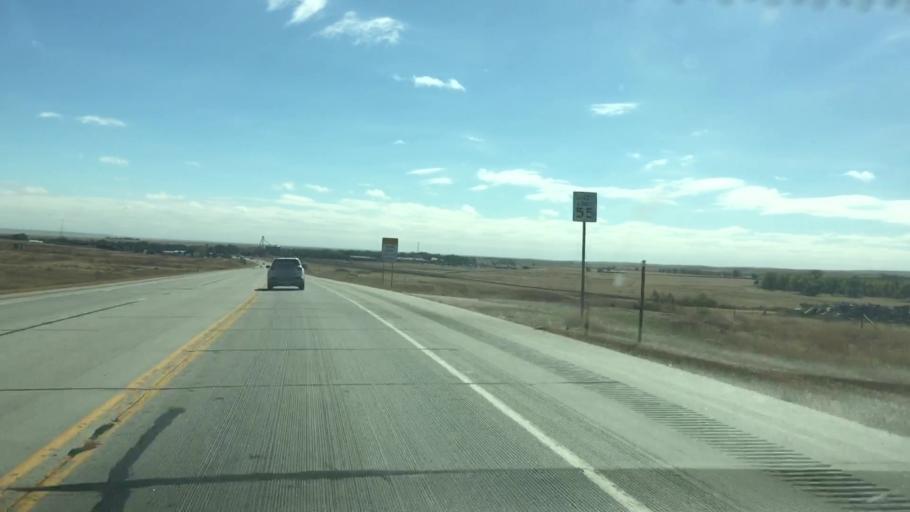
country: US
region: Colorado
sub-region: Lincoln County
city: Hugo
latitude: 39.1419
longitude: -103.4889
